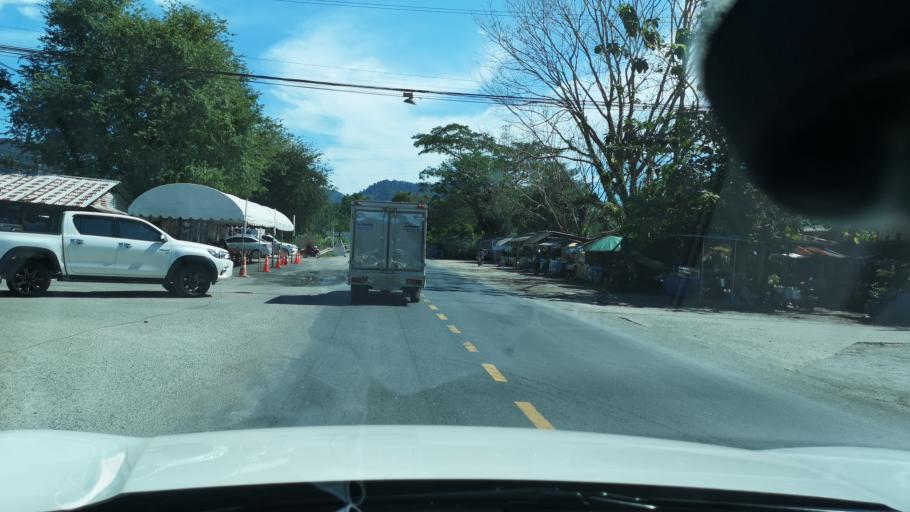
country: TH
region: Phangnga
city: Phang Nga
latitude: 8.5301
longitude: 98.5163
